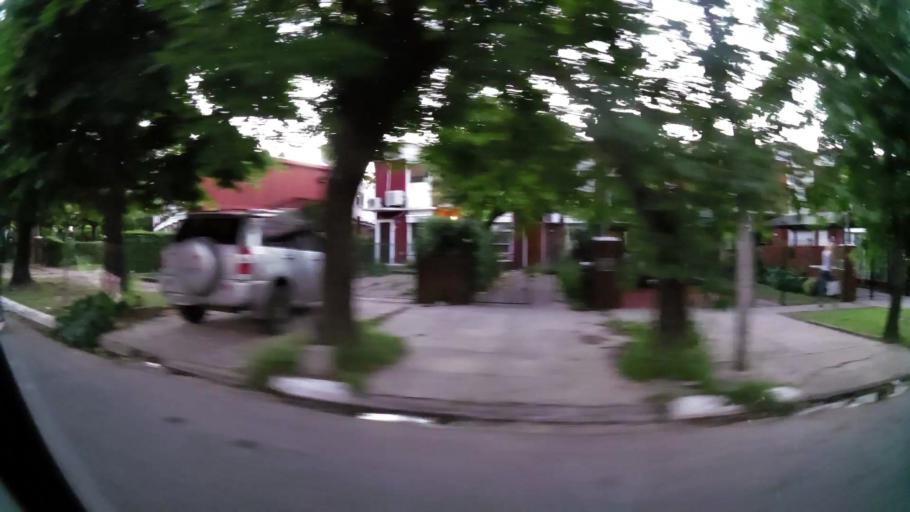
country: AR
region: Buenos Aires
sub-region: Partido de Quilmes
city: Quilmes
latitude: -34.8061
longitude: -58.1852
